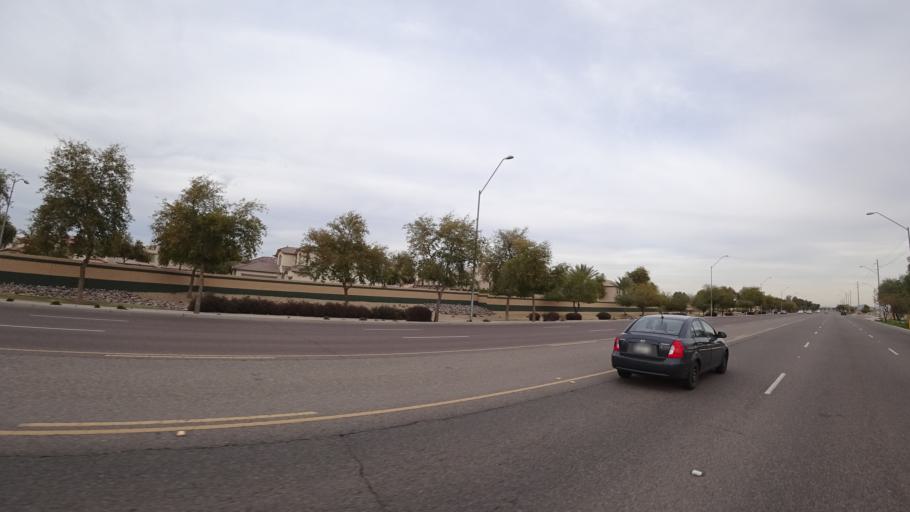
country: US
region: Arizona
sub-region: Maricopa County
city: El Mirage
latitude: 33.6091
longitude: -112.3530
